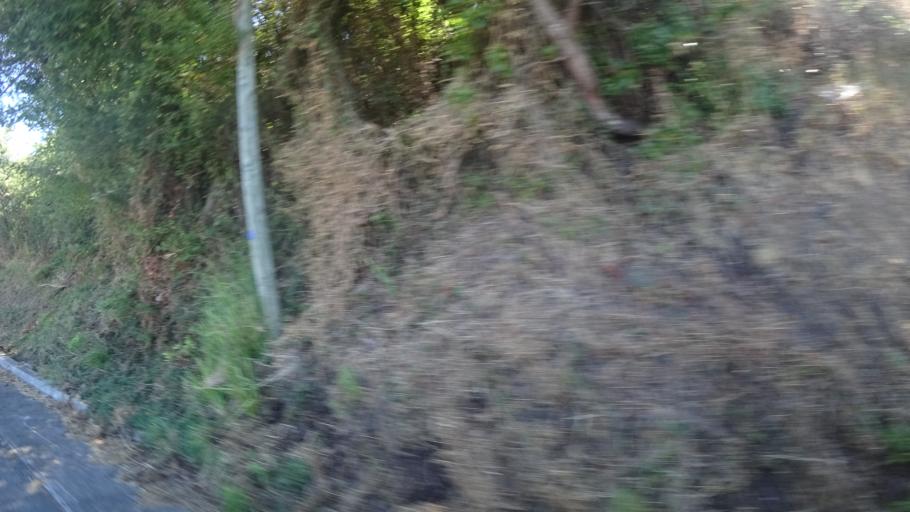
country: FR
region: Corsica
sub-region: Departement de la Corse-du-Sud
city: Alata
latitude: 41.9805
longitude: 8.6790
